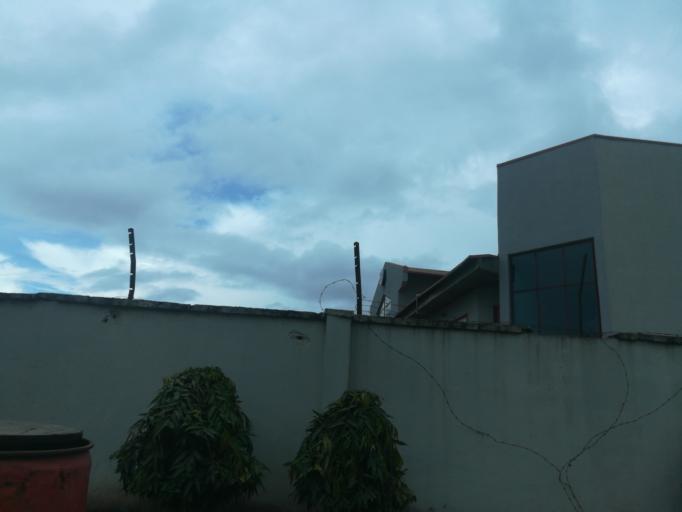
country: NG
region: Lagos
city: Agege
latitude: 6.6160
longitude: 3.3399
